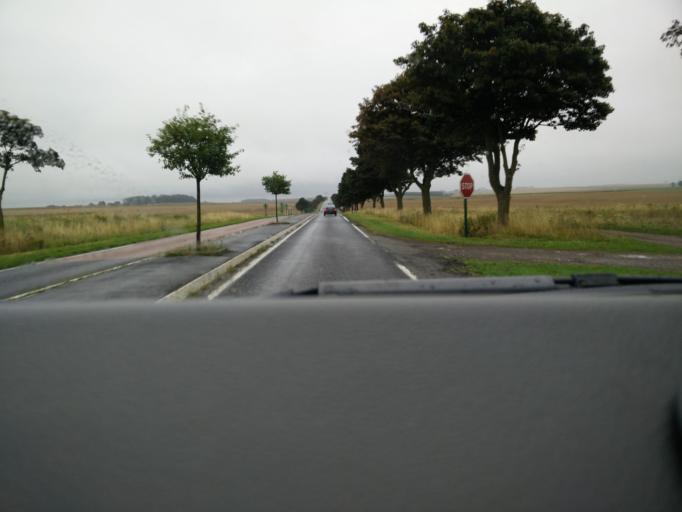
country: FR
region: Nord-Pas-de-Calais
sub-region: Departement du Pas-de-Calais
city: Saint-Pol-sur-Ternoise
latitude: 50.3919
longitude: 2.2230
